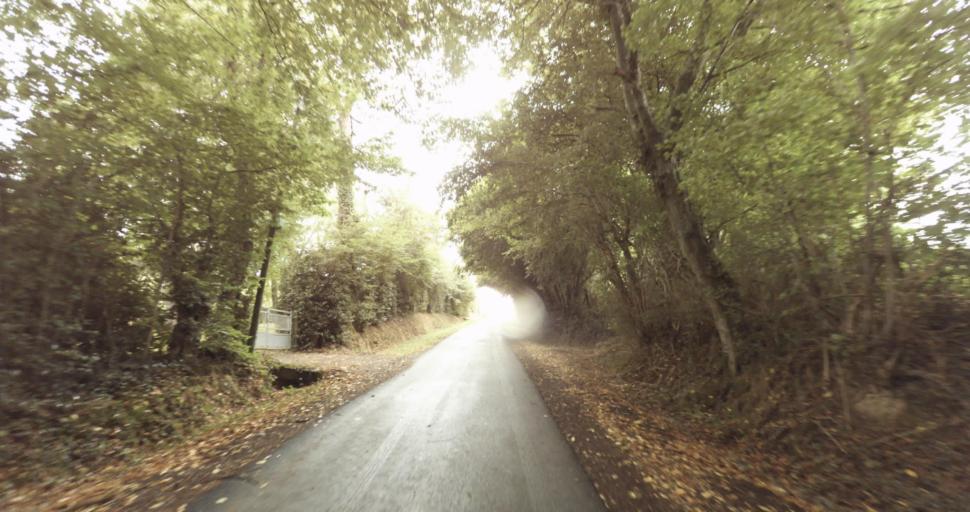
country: FR
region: Lower Normandy
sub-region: Departement de l'Orne
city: Sainte-Gauburge-Sainte-Colombe
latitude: 48.7254
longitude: 0.3975
